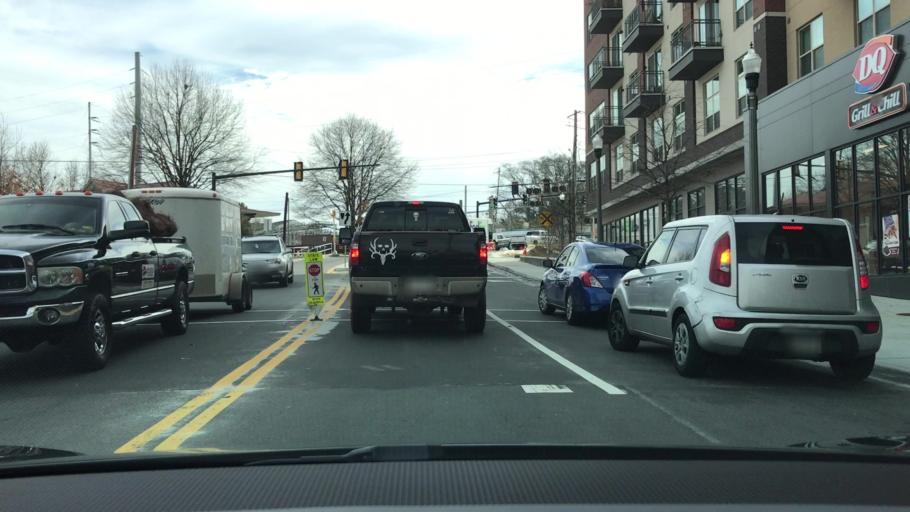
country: US
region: Georgia
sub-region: DeKalb County
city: Decatur
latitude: 33.7719
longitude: -84.2934
